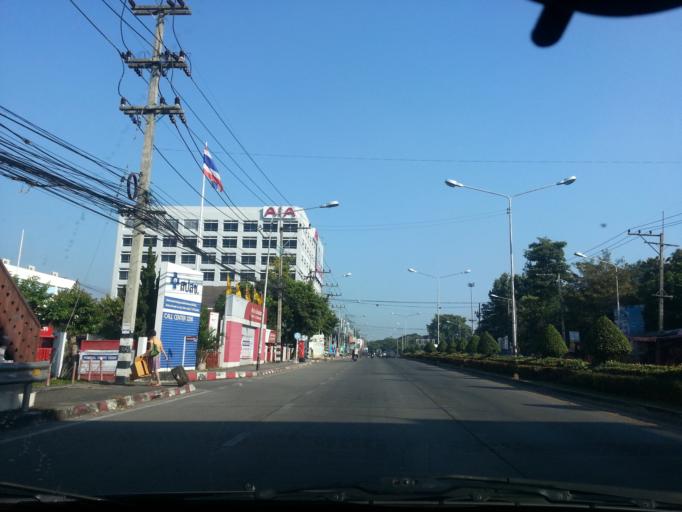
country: TH
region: Chiang Mai
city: Chiang Mai
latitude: 18.7796
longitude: 98.9771
